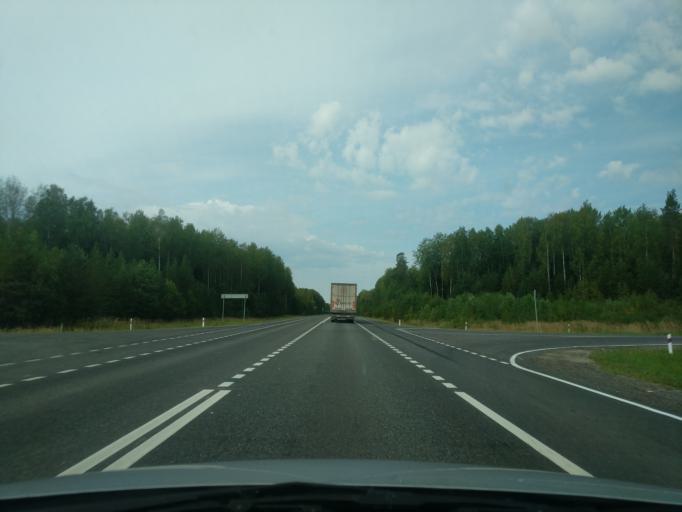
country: RU
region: Kirov
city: Leninskoye
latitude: 58.3189
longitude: 46.8768
